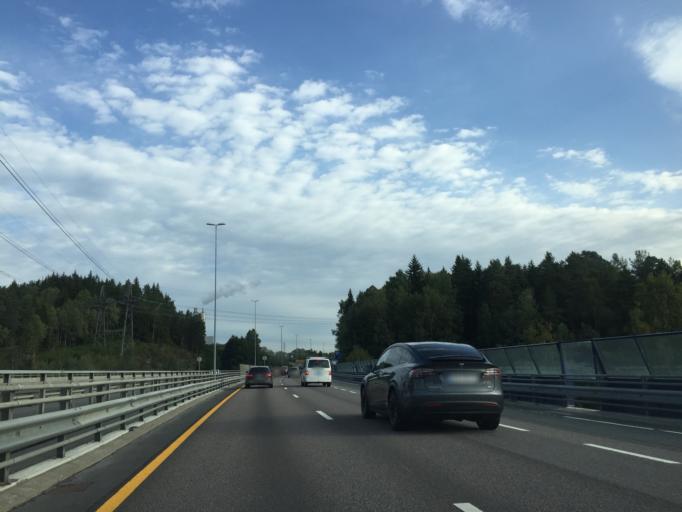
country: NO
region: Akershus
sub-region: Oppegard
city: Kolbotn
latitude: 59.8346
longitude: 10.8398
